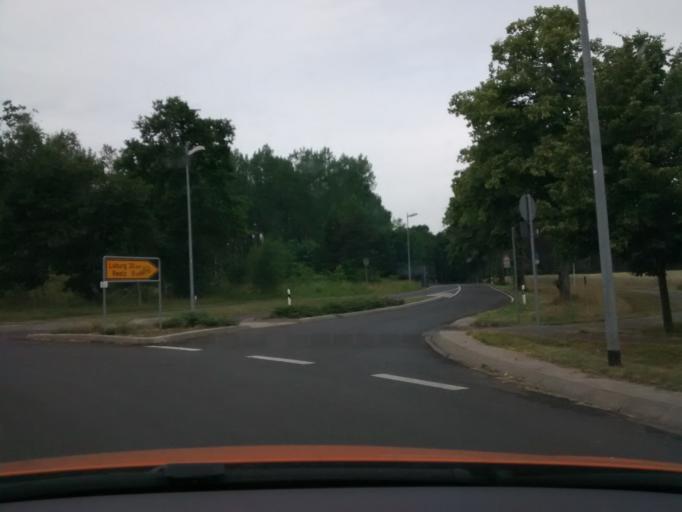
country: DE
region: Brandenburg
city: Wiesenburg
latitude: 52.1107
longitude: 12.4411
